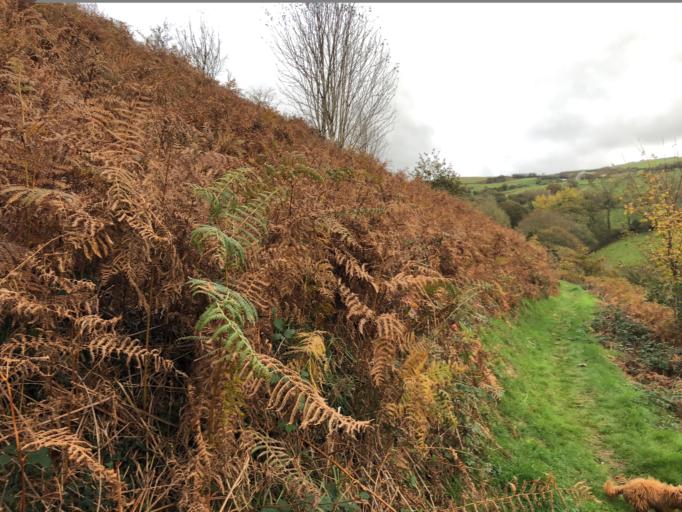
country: GB
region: Wales
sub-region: Gwynedd
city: Tywyn
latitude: 52.5500
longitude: -4.0377
